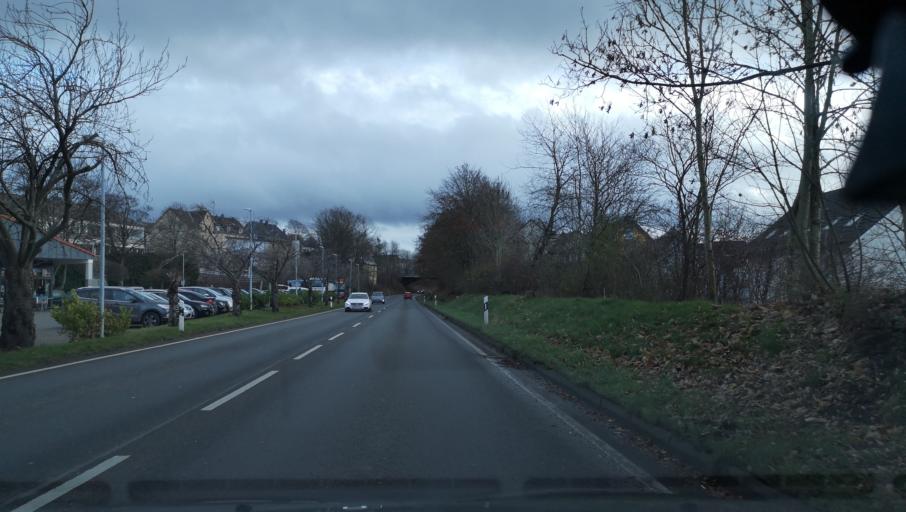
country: DE
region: North Rhine-Westphalia
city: Radevormwald
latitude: 51.2009
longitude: 7.3625
